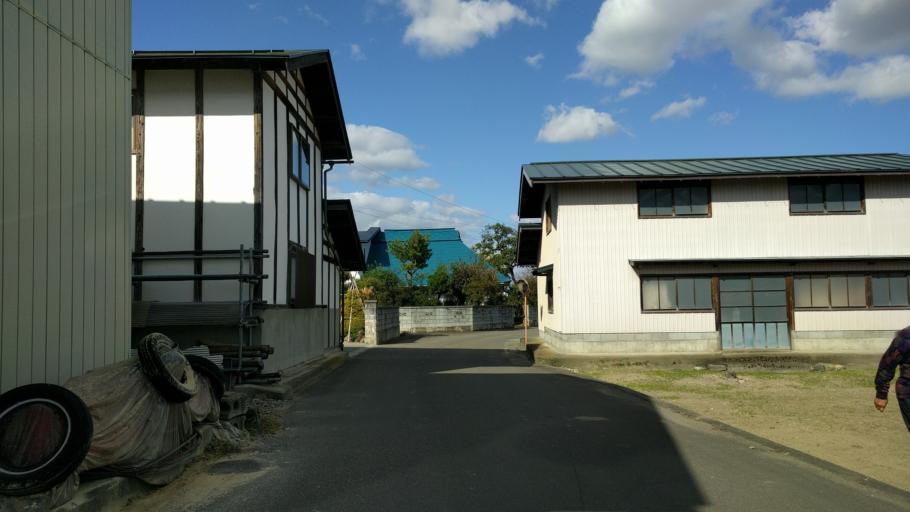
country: JP
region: Fukushima
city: Kitakata
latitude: 37.4519
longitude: 139.8454
